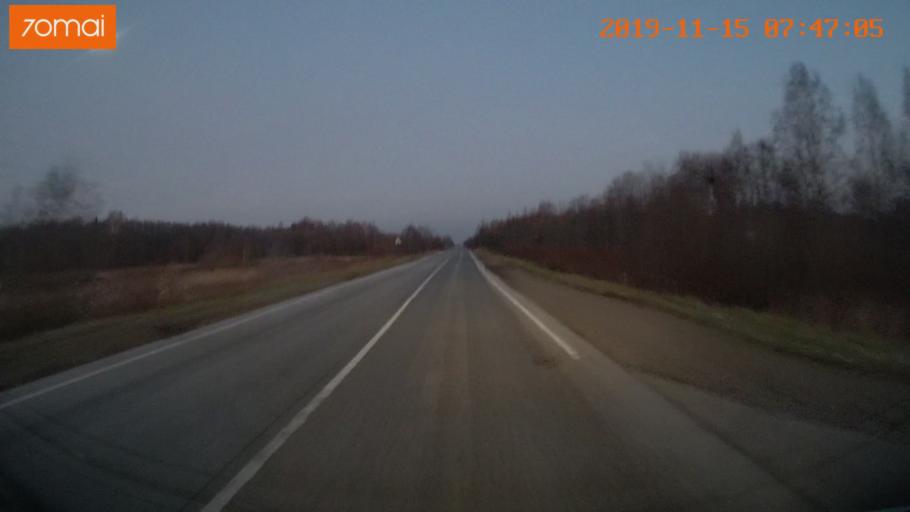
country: RU
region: Vologda
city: Sheksna
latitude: 58.8378
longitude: 38.2681
